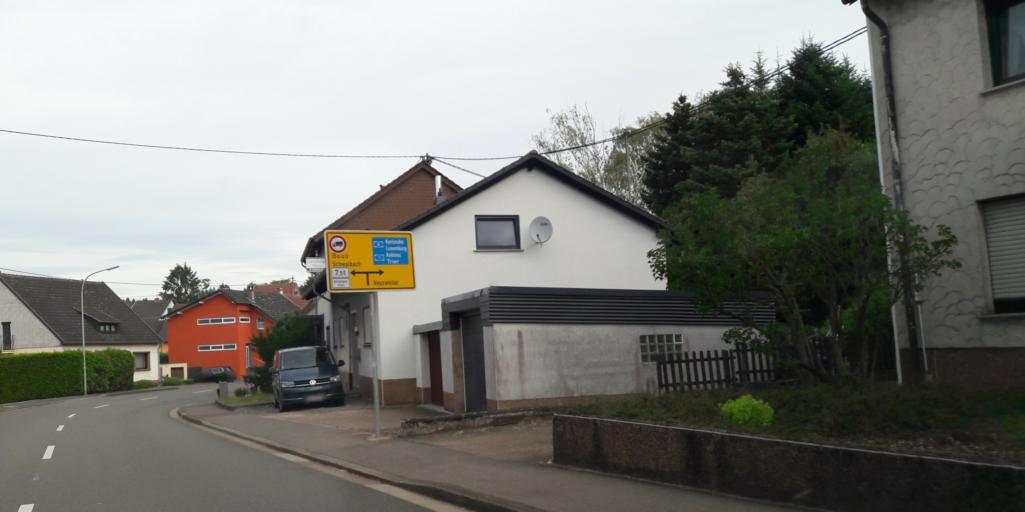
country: DE
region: Saarland
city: Puttlingen
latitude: 49.3063
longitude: 6.8555
